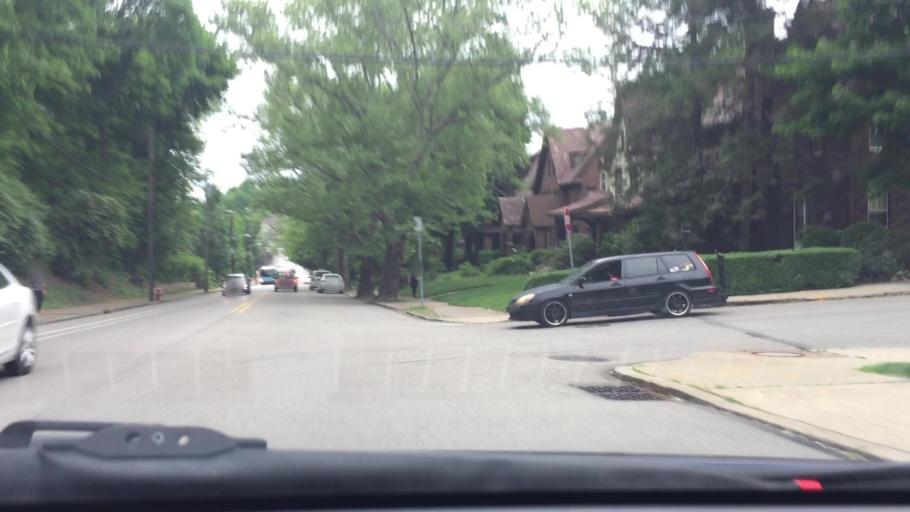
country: US
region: Pennsylvania
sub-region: Allegheny County
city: Bloomfield
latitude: 40.4405
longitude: -79.9355
